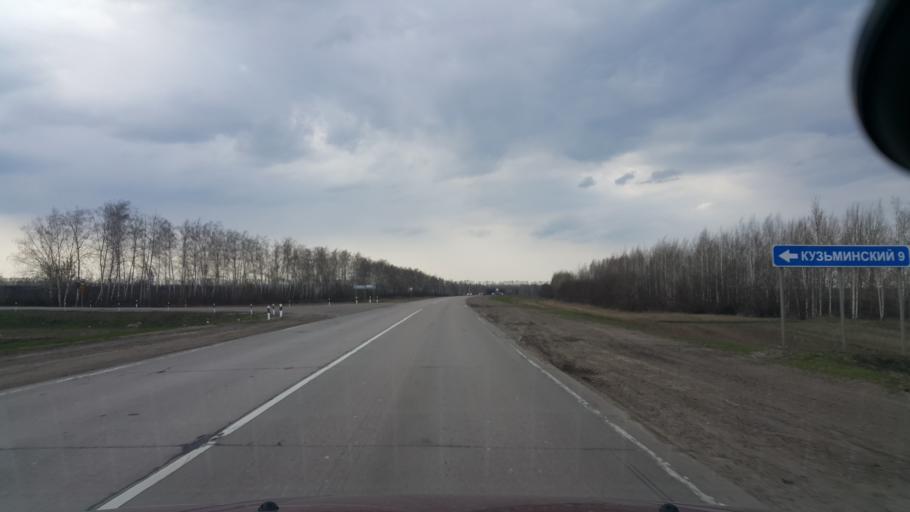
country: RU
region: Tambov
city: Znamenka
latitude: 52.4116
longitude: 41.3809
